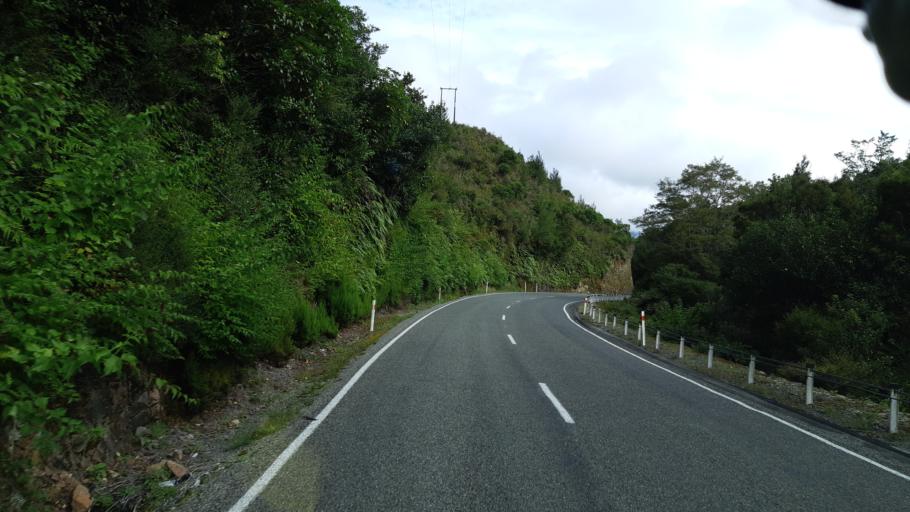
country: NZ
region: West Coast
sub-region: Buller District
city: Westport
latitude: -41.9868
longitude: 172.2100
